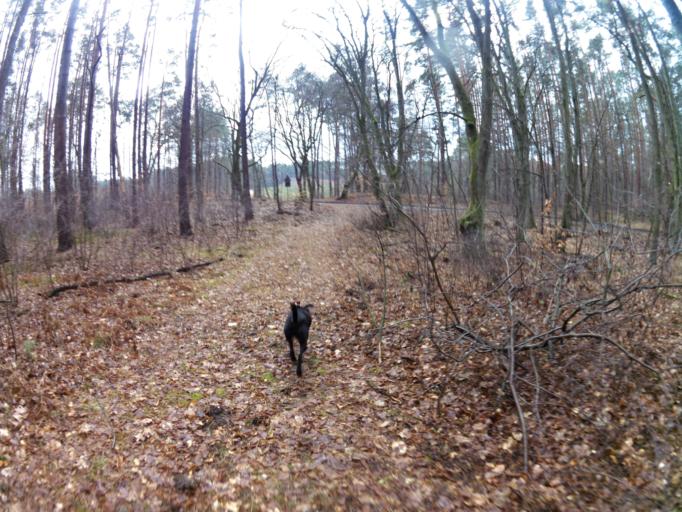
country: PL
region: West Pomeranian Voivodeship
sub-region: Powiat mysliborski
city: Debno
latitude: 52.7220
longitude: 14.7296
